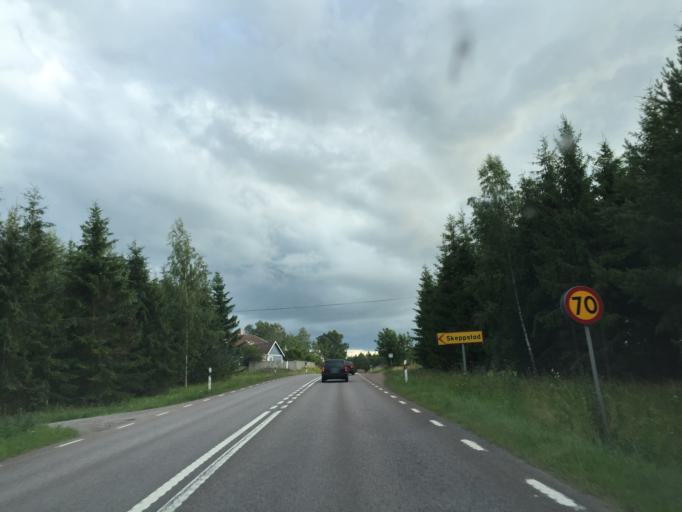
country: SE
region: OEstergoetland
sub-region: Motala Kommun
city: Motala
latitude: 58.4863
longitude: 14.9901
